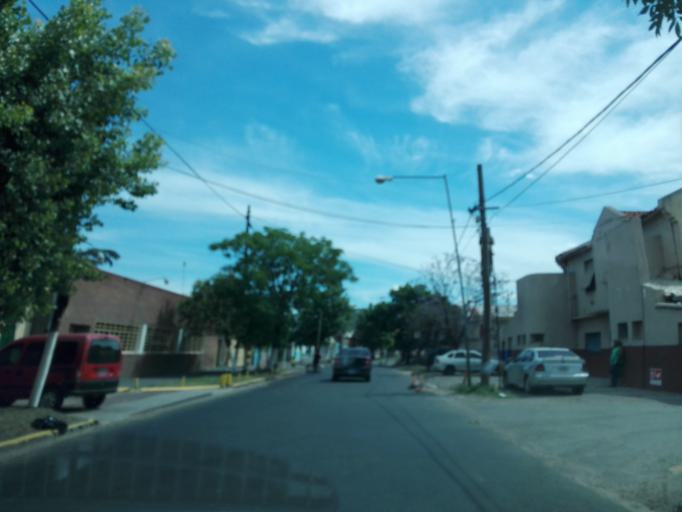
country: AR
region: Buenos Aires
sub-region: Partido de Lanus
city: Lanus
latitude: -34.7043
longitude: -58.3680
